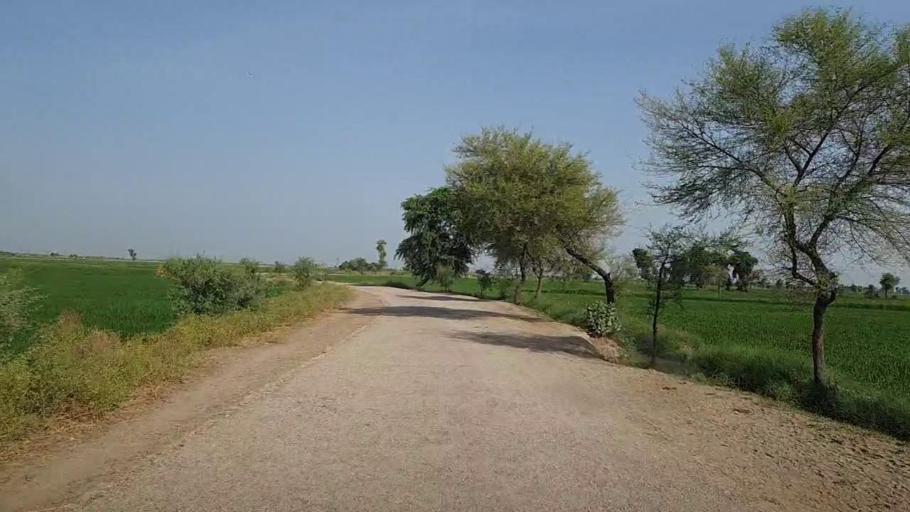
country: PK
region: Sindh
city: Sita Road
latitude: 27.1084
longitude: 67.8482
